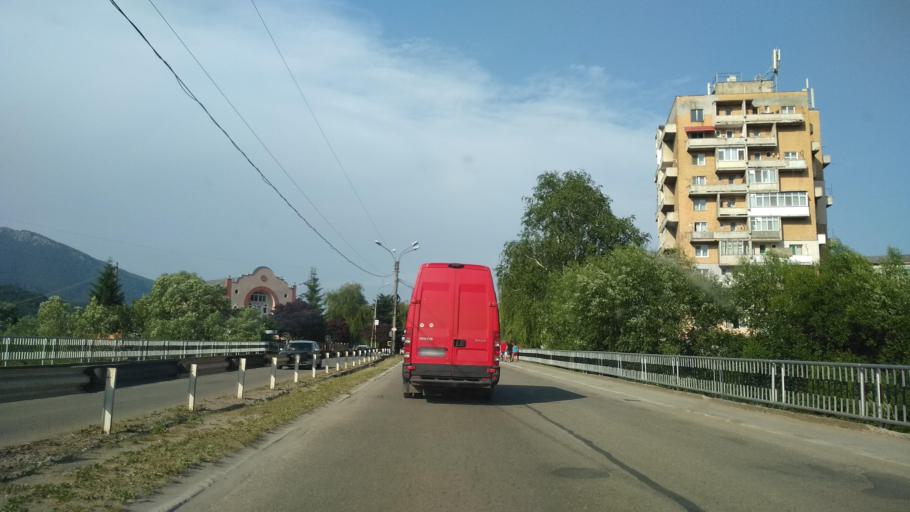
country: RO
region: Hunedoara
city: Lupeni
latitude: 45.3492
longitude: 23.1989
